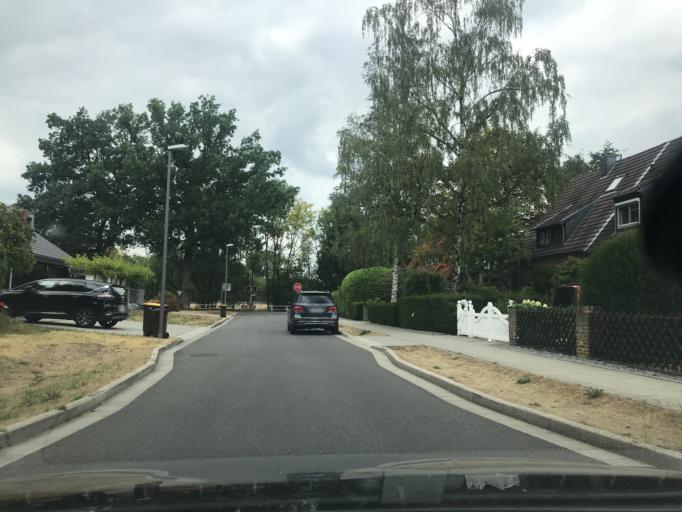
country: DE
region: North Rhine-Westphalia
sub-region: Regierungsbezirk Dusseldorf
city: Krefeld
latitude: 51.3566
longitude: 6.5622
